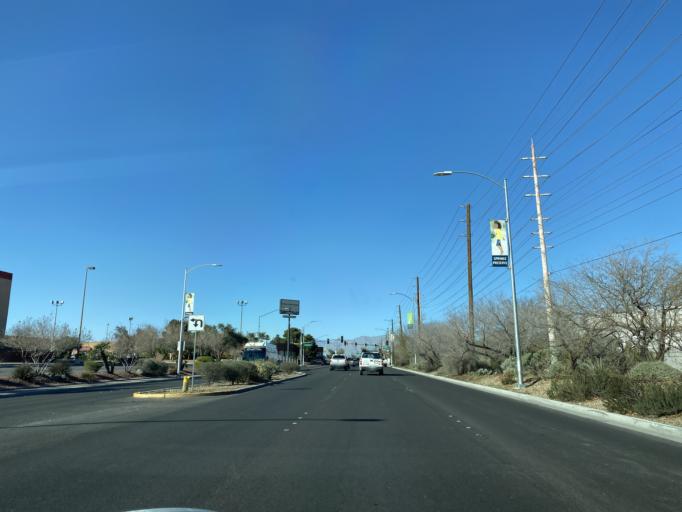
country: US
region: Nevada
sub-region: Clark County
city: Las Vegas
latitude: 36.1686
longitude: -115.1925
